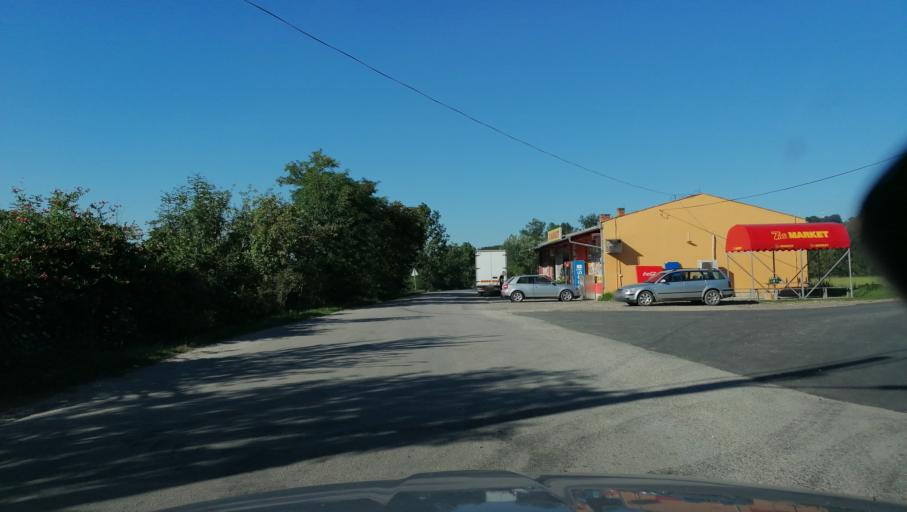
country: RS
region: Central Serbia
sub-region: Sumadijski Okrug
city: Knic
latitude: 43.8425
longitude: 20.6008
